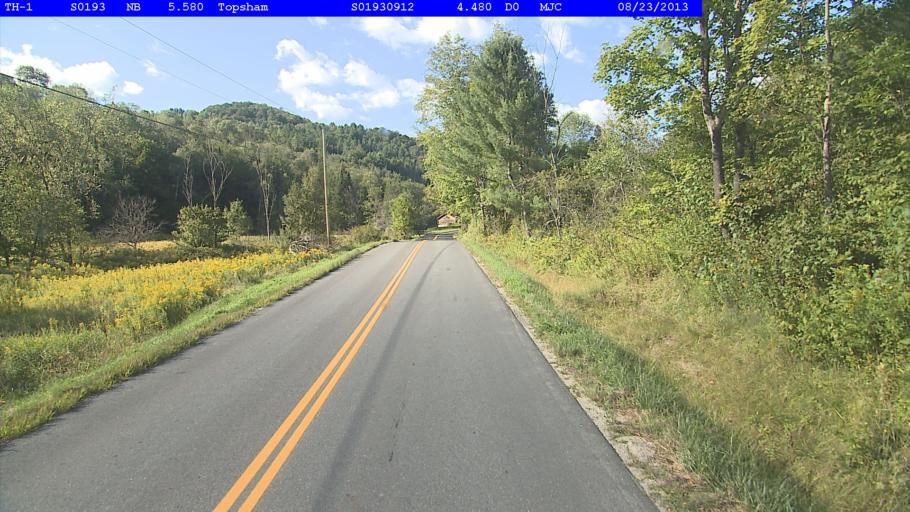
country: US
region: New Hampshire
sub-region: Grafton County
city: Haverhill
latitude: 44.1280
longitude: -72.2430
